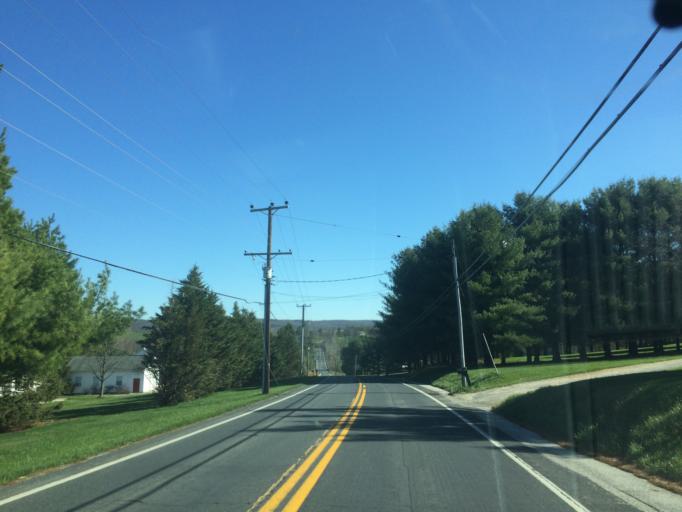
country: US
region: Maryland
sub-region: Carroll County
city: Manchester
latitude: 39.6575
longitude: -76.9506
